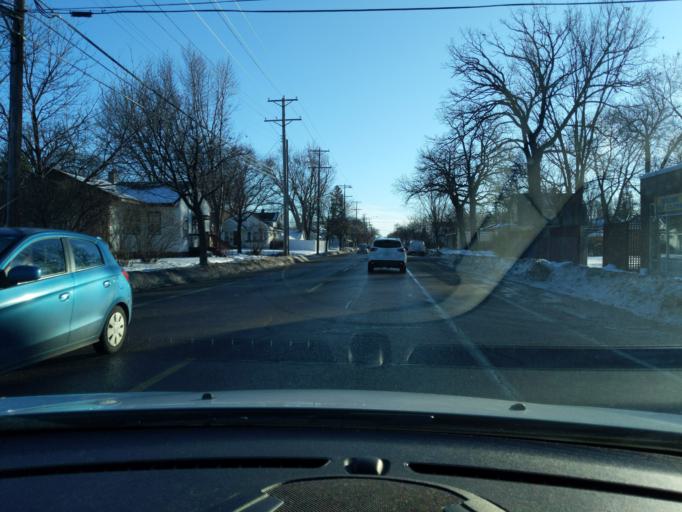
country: US
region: Minnesota
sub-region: Hennepin County
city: Minneapolis
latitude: 44.9269
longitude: -93.2304
